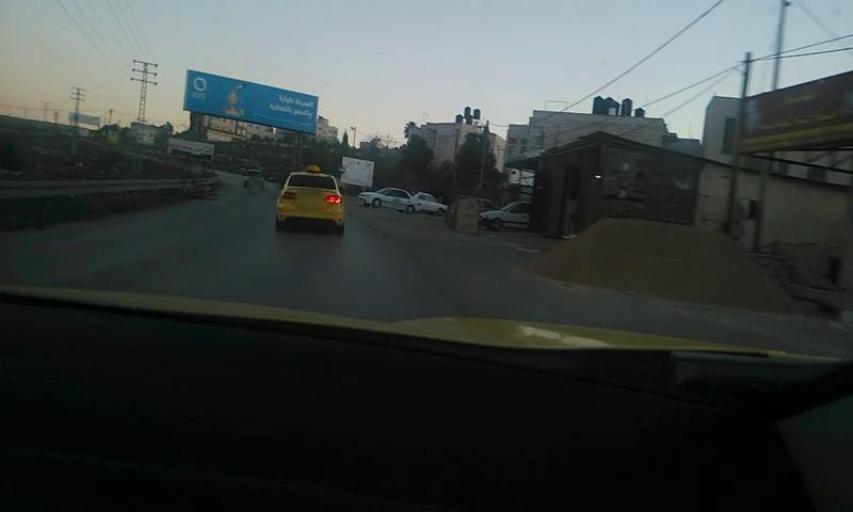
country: PS
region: West Bank
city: Surda
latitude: 31.9433
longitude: 35.2149
